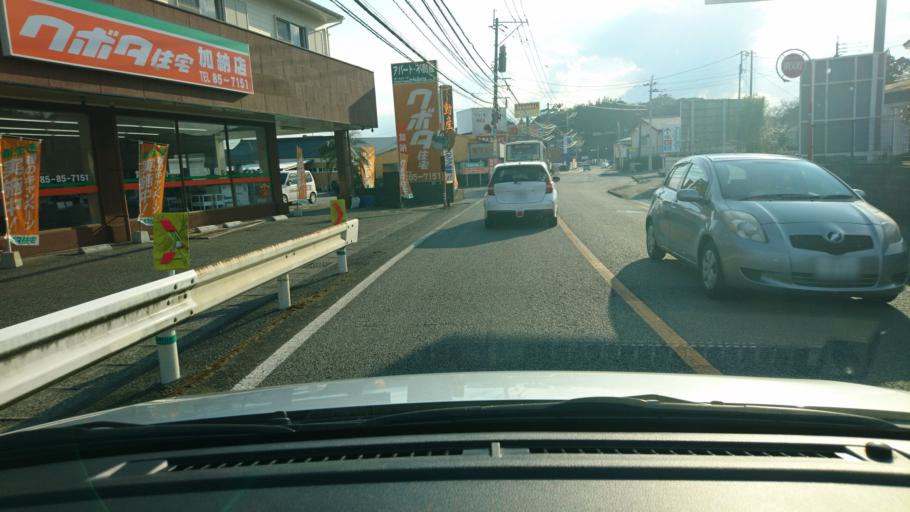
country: JP
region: Miyazaki
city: Miyazaki-shi
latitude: 31.8811
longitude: 131.4077
